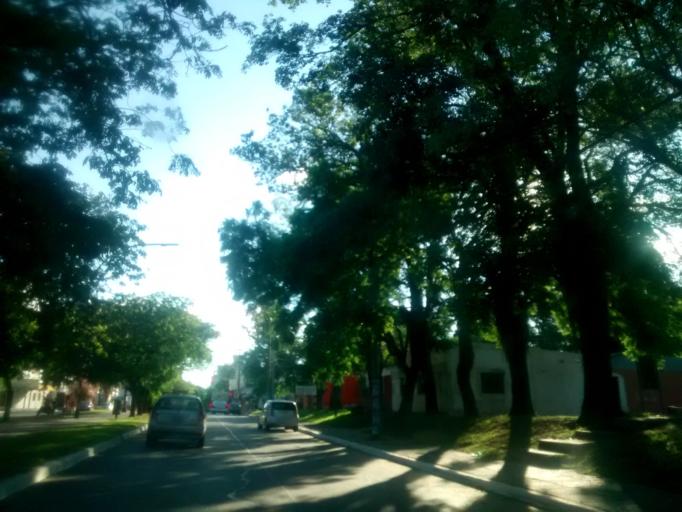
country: AR
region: Chaco
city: Resistencia
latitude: -27.4419
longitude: -58.9763
